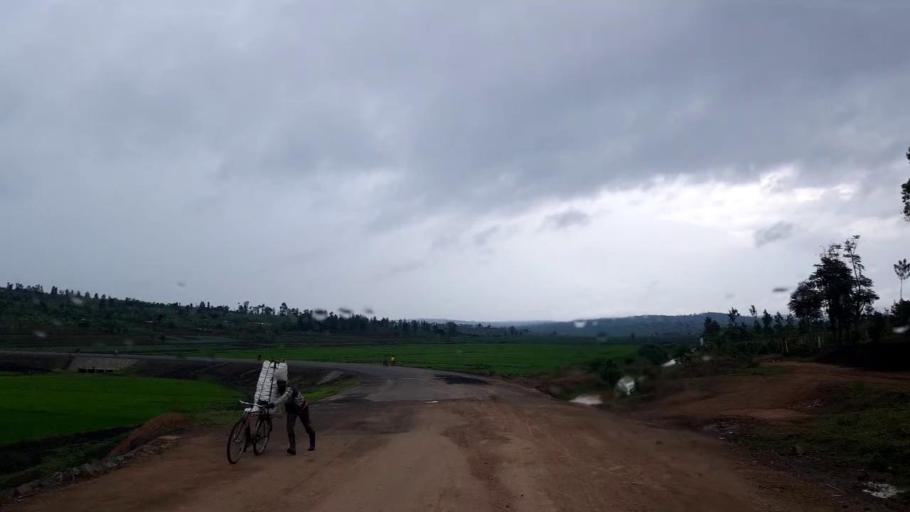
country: RW
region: Northern Province
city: Byumba
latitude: -1.4268
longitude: 30.2728
